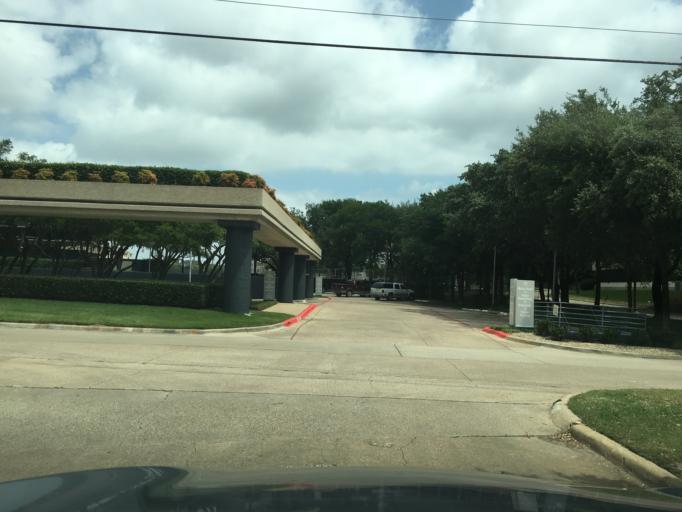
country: US
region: Texas
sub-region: Dallas County
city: Addison
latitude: 32.9339
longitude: -96.8164
